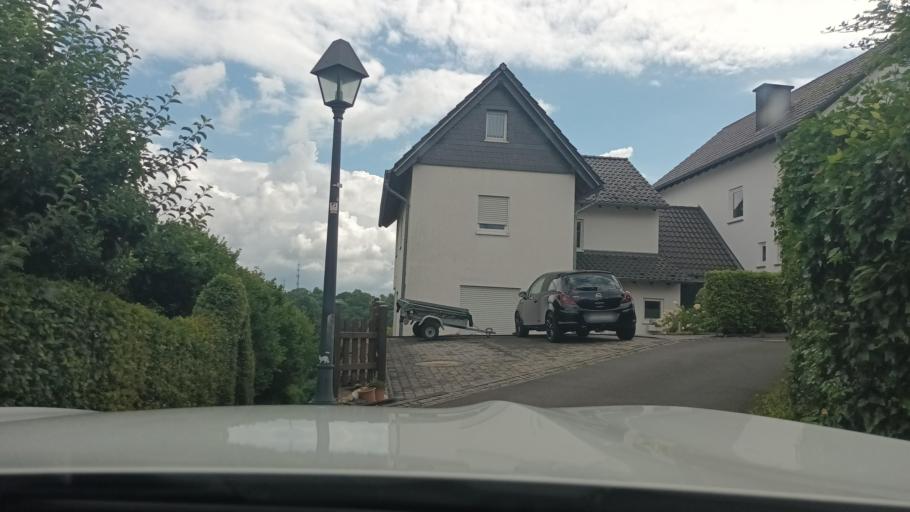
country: DE
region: North Rhine-Westphalia
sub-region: Regierungsbezirk Koln
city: Hennef
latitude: 50.7631
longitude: 7.3636
